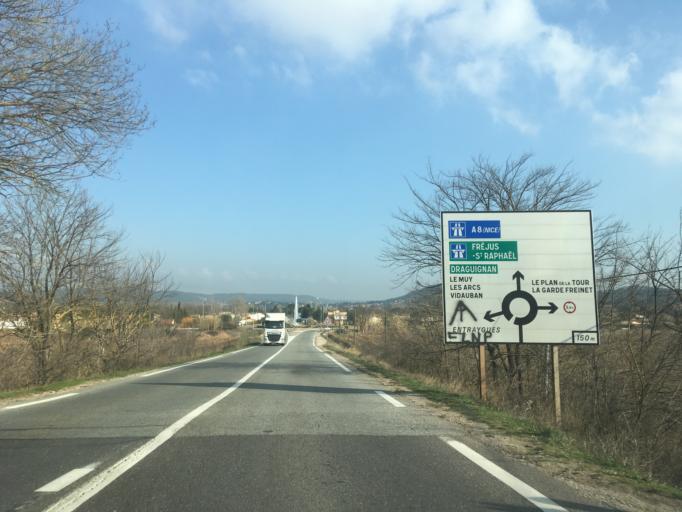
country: FR
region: Provence-Alpes-Cote d'Azur
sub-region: Departement du Var
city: Vidauban
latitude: 43.4124
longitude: 6.4170
